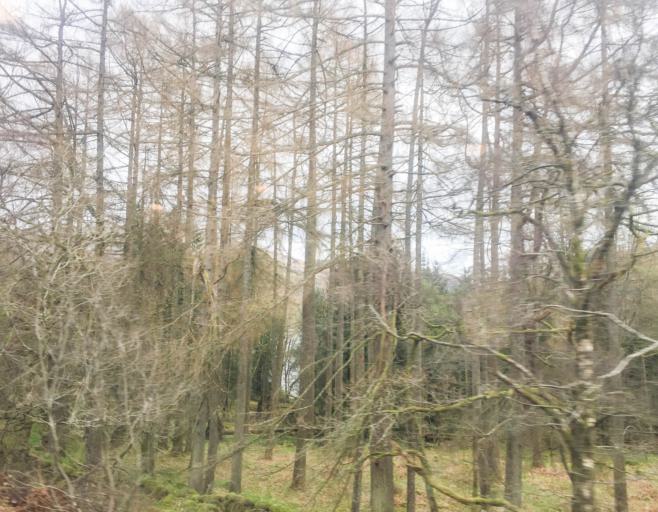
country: GB
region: Scotland
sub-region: Argyll and Bute
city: Garelochhead
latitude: 56.2499
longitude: -4.7146
